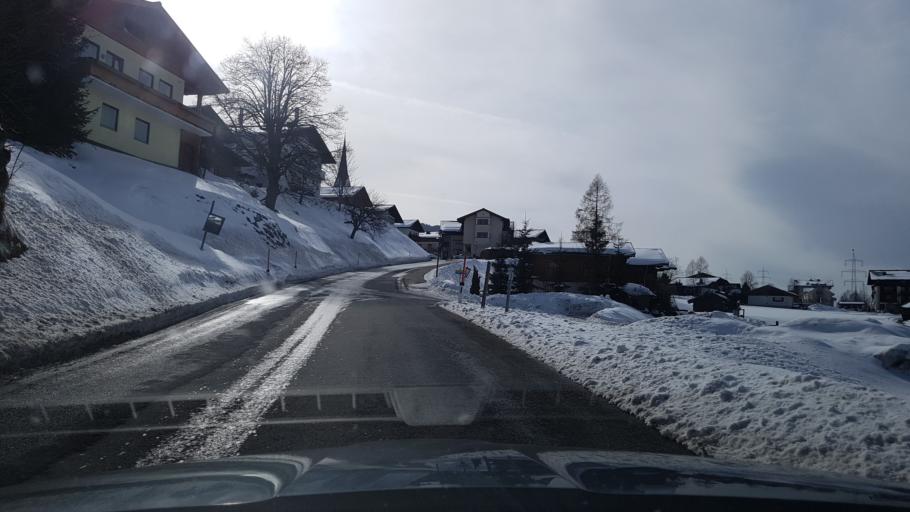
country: AT
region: Salzburg
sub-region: Politischer Bezirk Zell am See
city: Taxenbach
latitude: 47.2913
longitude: 13.0046
